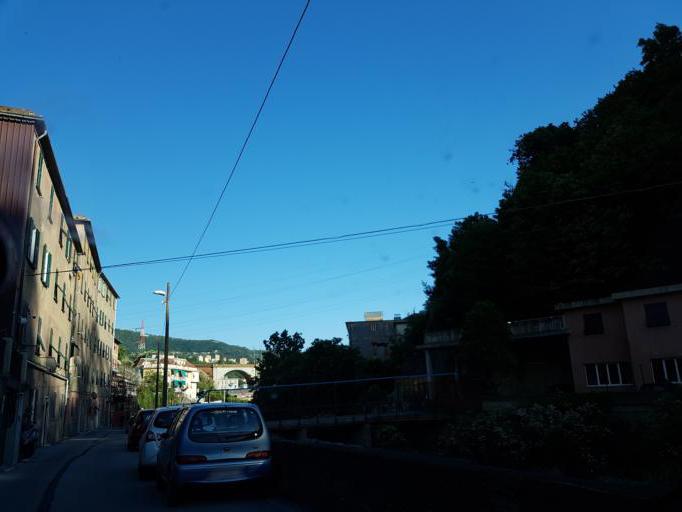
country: IT
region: Liguria
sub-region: Provincia di Genova
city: Genoa
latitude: 44.4562
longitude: 8.8879
